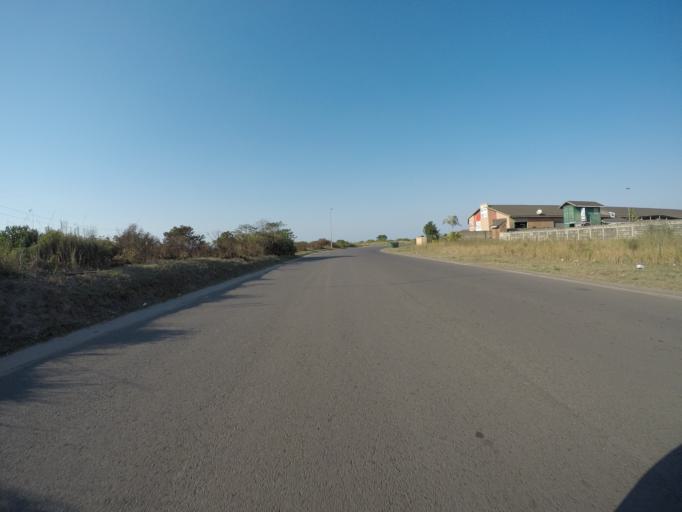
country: ZA
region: KwaZulu-Natal
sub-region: uThungulu District Municipality
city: Richards Bay
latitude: -28.7357
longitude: 32.0393
